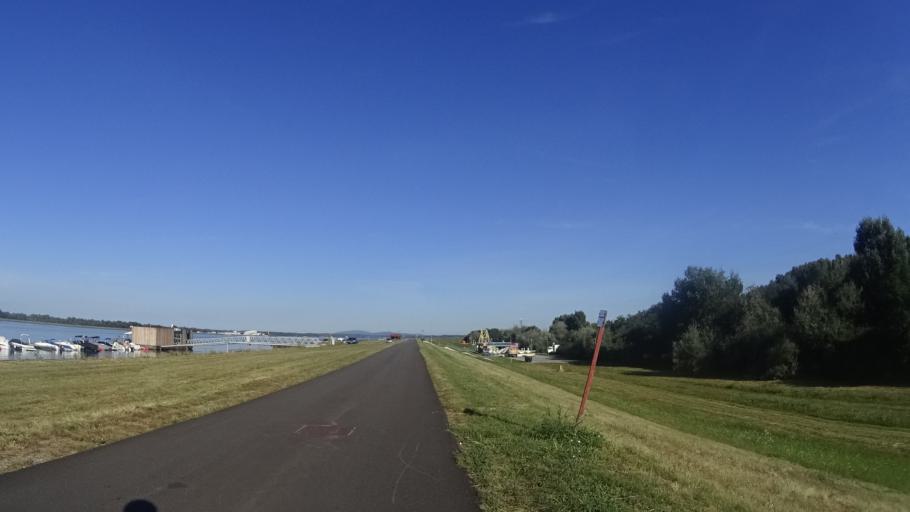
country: SK
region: Bratislavsky
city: Dunajska Luzna
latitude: 48.0316
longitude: 17.2518
